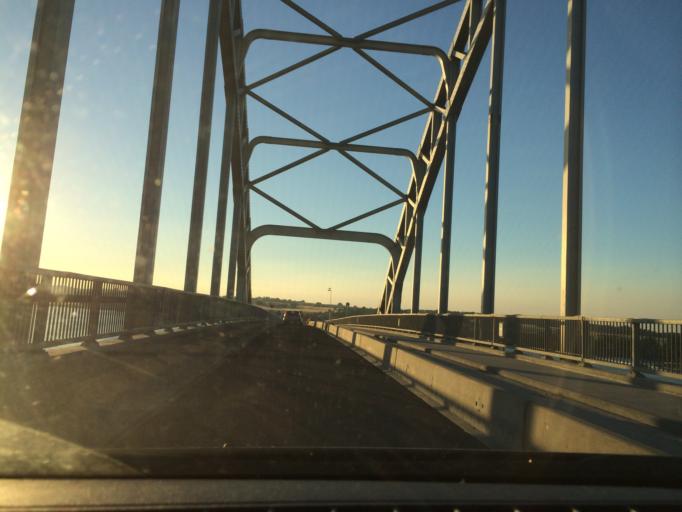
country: DK
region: Zealand
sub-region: Vordingborg Kommune
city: Stege
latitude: 54.9893
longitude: 12.1648
